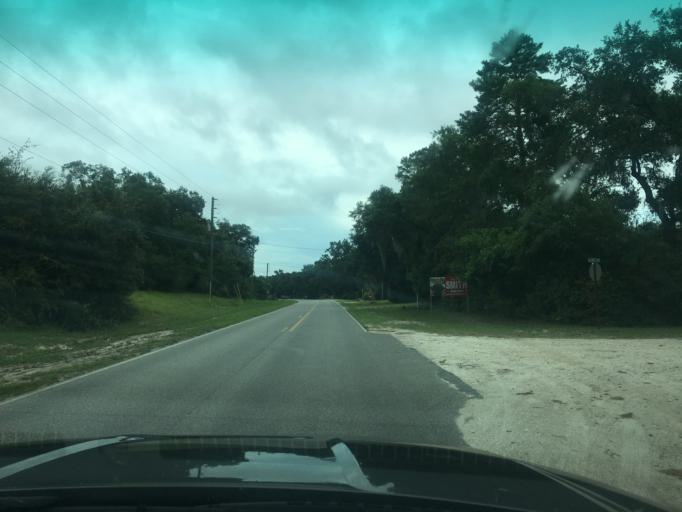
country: US
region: Florida
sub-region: Wakulla County
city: Crawfordville
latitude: 29.9143
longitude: -84.3674
